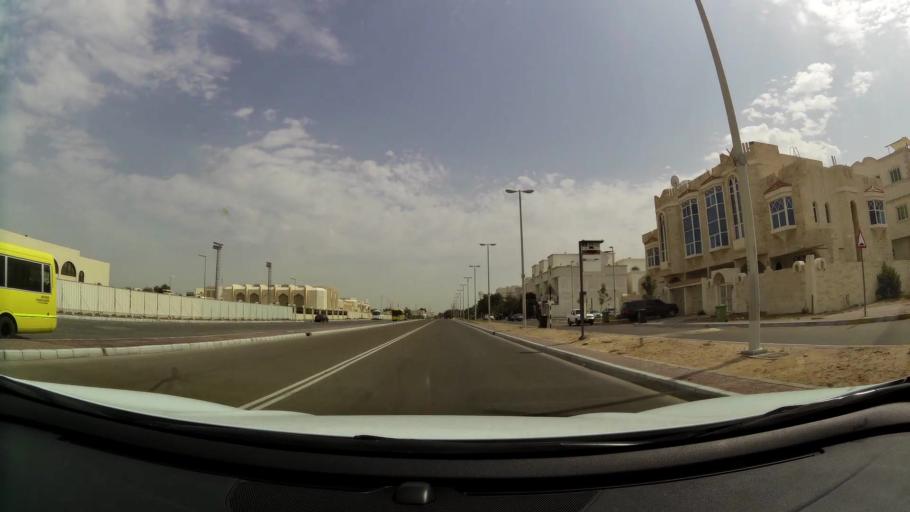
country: AE
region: Abu Dhabi
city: Abu Dhabi
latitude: 24.4612
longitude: 54.3424
